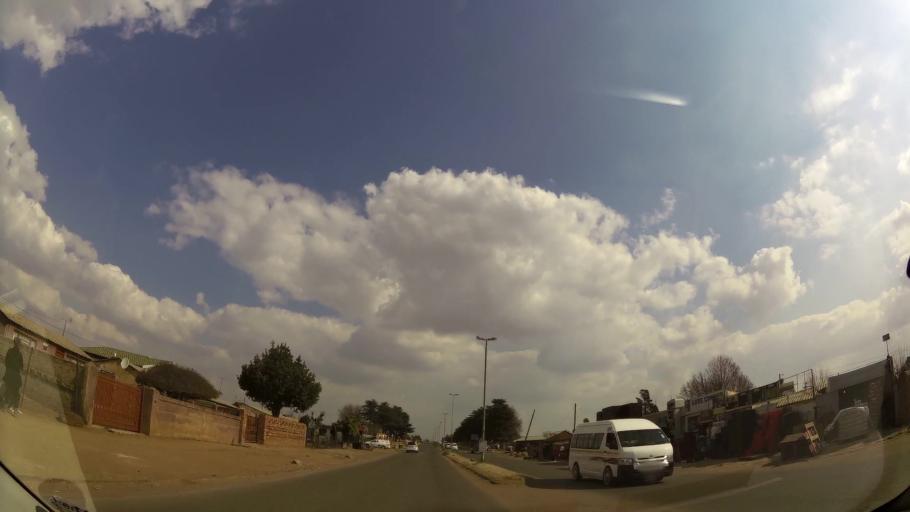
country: ZA
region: Gauteng
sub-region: Ekurhuleni Metropolitan Municipality
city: Springs
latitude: -26.1278
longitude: 28.4438
